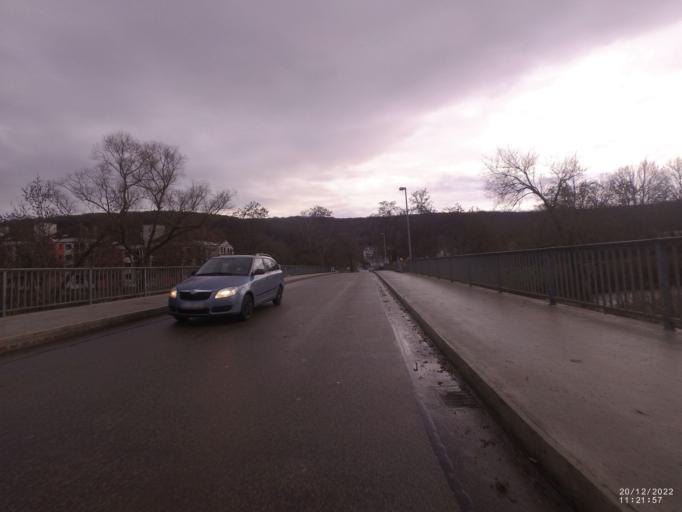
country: DE
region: Rheinland-Pfalz
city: Remagen
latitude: 50.5509
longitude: 7.2175
